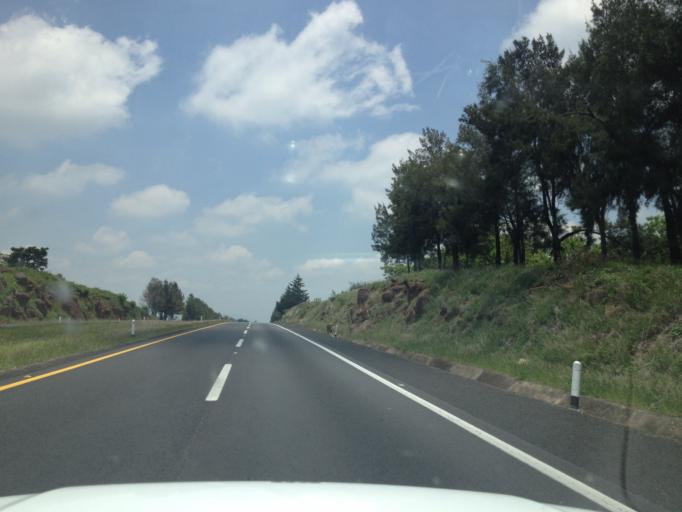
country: MX
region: Michoacan
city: Penjamillo de Degollado
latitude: 20.0817
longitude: -101.9858
